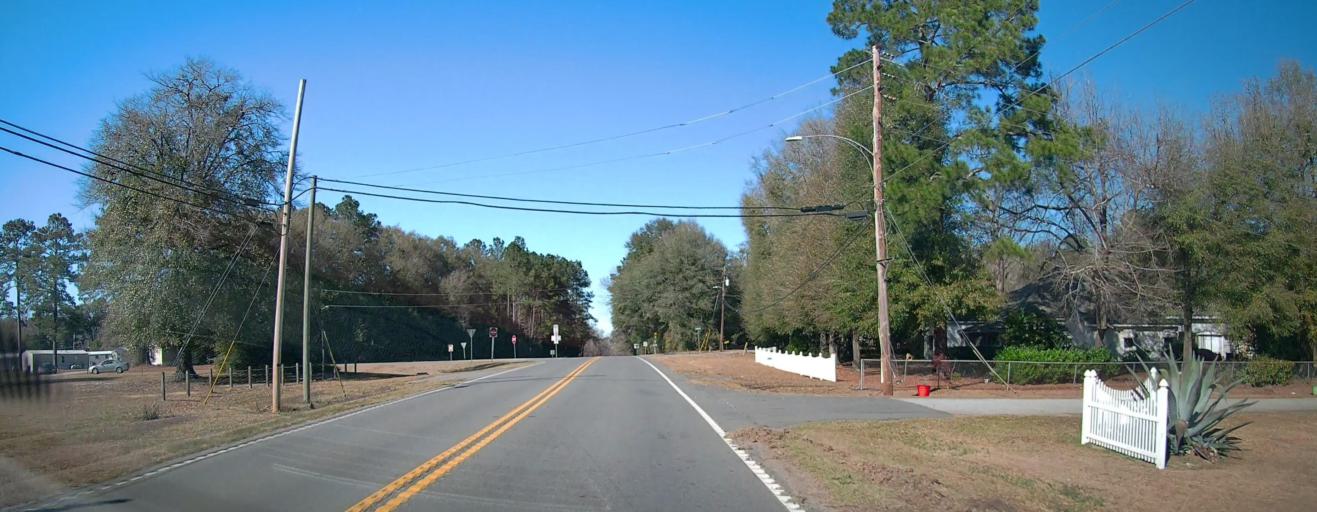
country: US
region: Georgia
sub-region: Macon County
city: Oglethorpe
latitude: 32.3050
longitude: -84.0656
